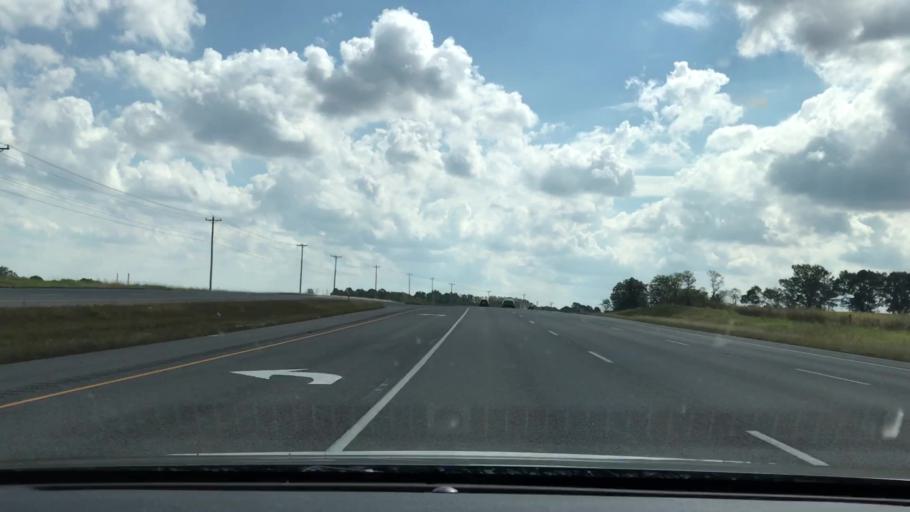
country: US
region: Kentucky
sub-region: Christian County
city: Oak Grove
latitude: 36.6864
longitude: -87.4510
